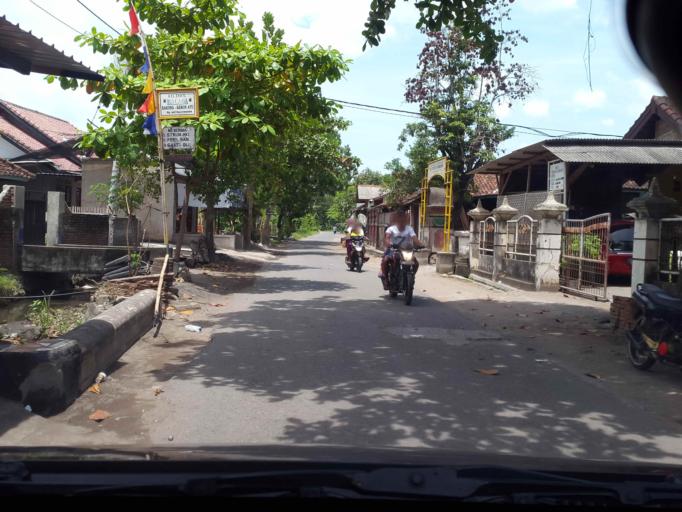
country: ID
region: West Nusa Tenggara
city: Jelateng Timur
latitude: -8.6844
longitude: 116.0910
